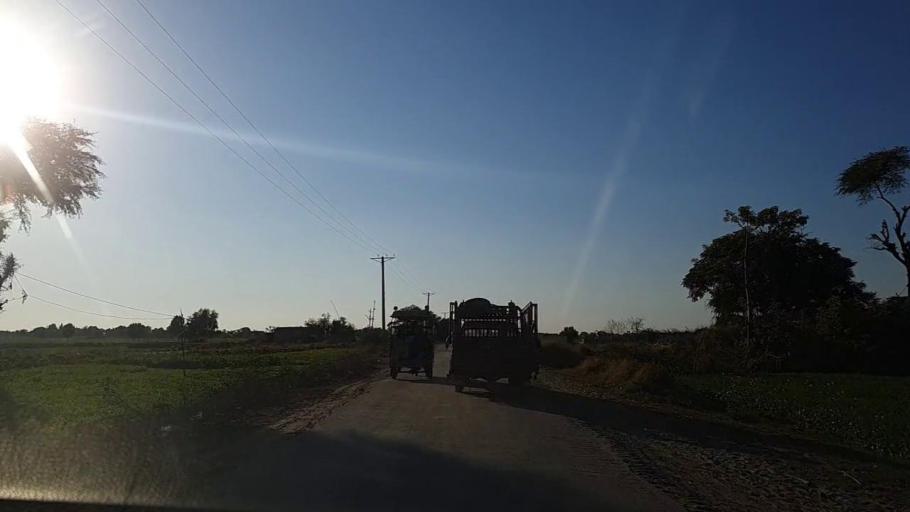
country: PK
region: Sindh
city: Sanghar
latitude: 26.2790
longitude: 68.9284
